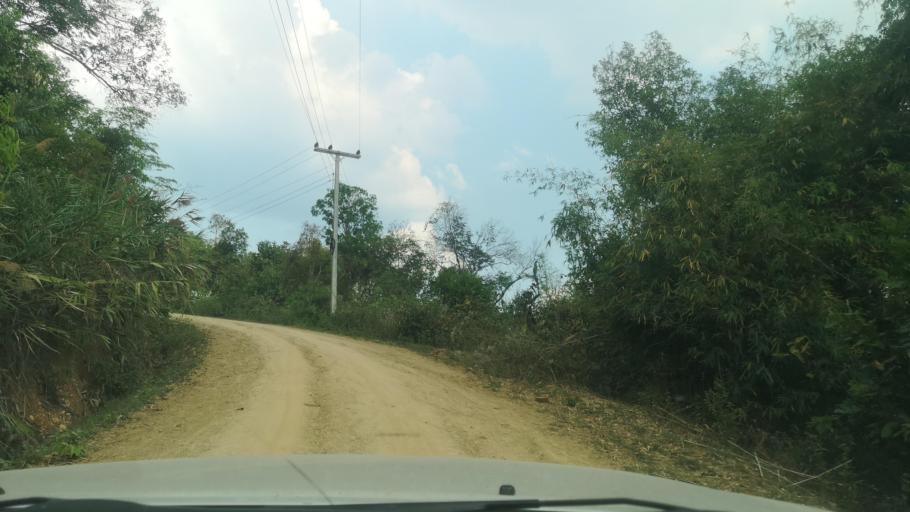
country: LA
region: Loungnamtha
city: Muang Nale
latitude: 20.2900
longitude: 101.3665
